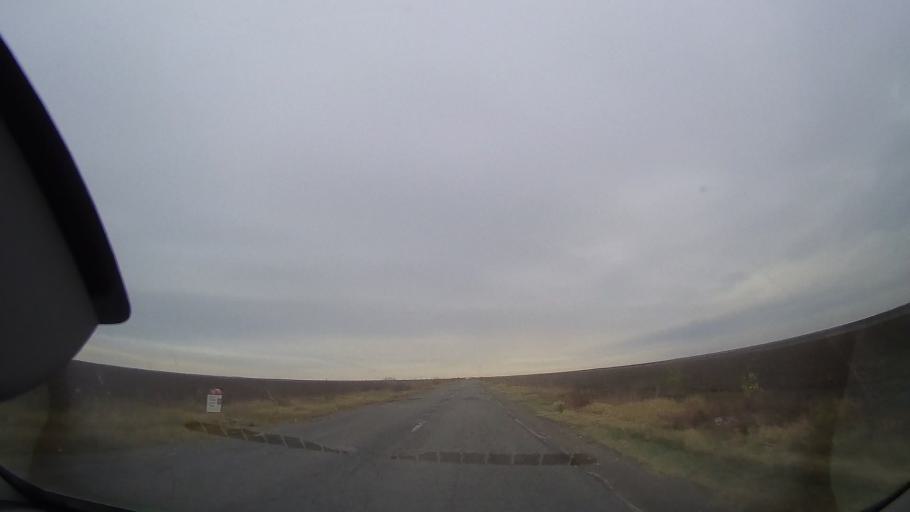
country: RO
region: Ialomita
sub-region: Oras Amara
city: Amara
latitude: 44.6527
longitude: 27.3006
